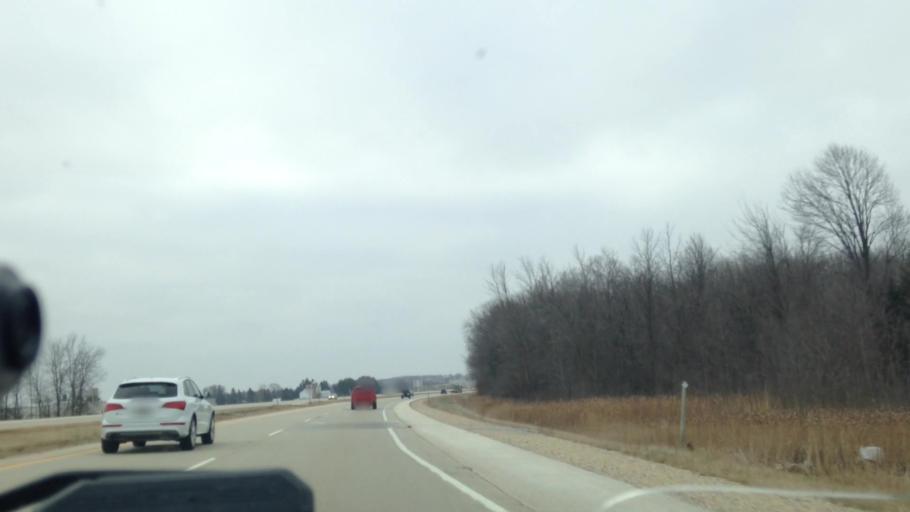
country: US
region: Wisconsin
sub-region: Washington County
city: Jackson
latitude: 43.3186
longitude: -88.1849
